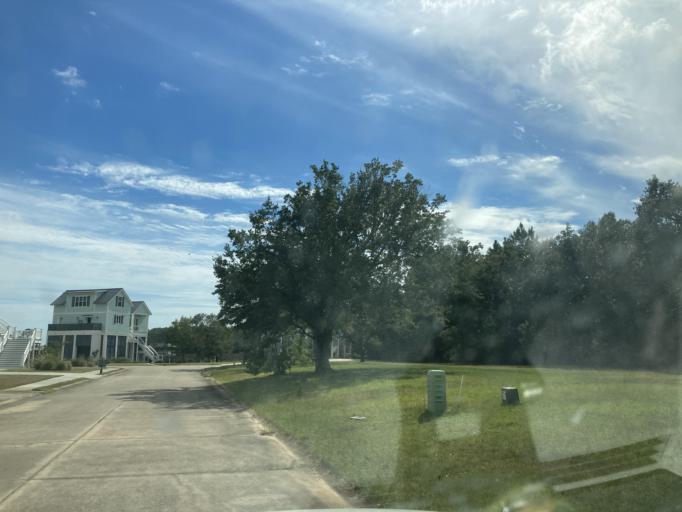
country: US
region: Mississippi
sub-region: Jackson County
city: Saint Martin
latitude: 30.4361
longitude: -88.8743
